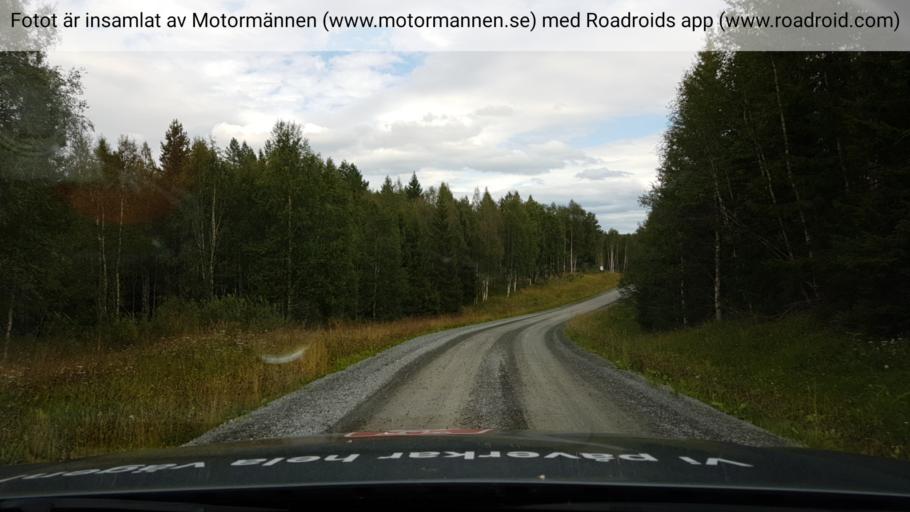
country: SE
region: Jaemtland
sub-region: Krokoms Kommun
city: Valla
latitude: 63.7072
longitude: 13.5845
